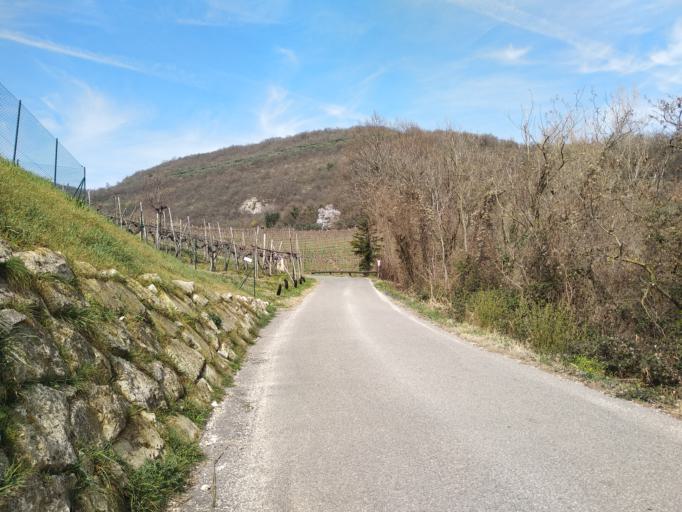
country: IT
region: Veneto
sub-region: Provincia di Vicenza
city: Barbarano Vicentino
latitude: 45.4129
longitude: 11.5433
